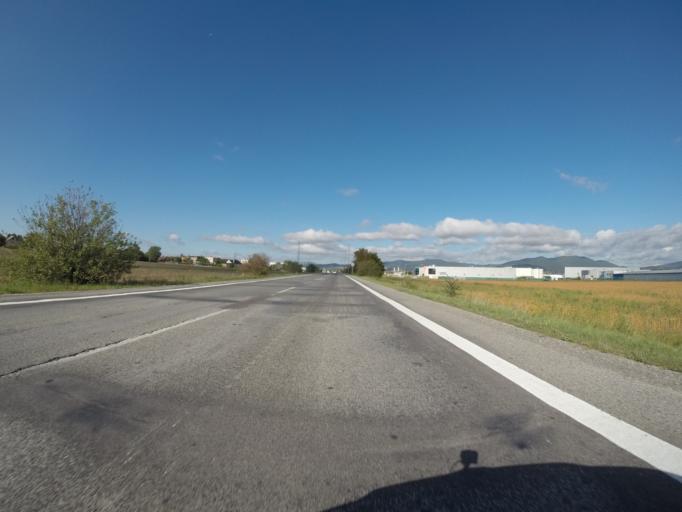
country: SK
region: Trenciansky
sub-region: Okres Trencin
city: Trencin
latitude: 48.8480
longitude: 17.9983
